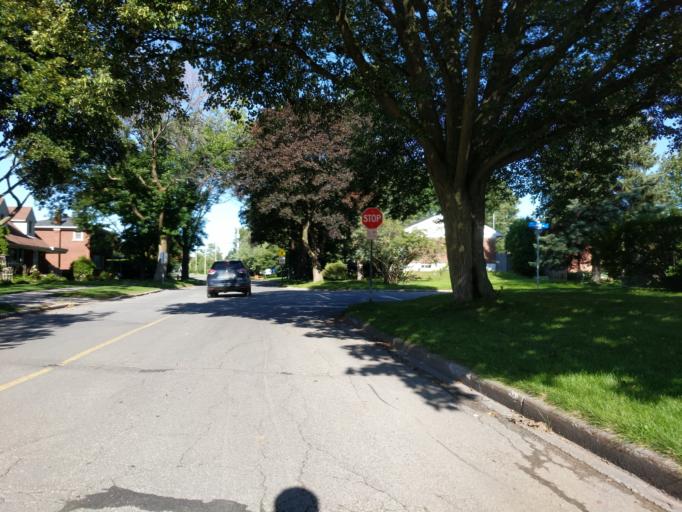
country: CA
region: Ontario
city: Bells Corners
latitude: 45.3616
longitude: -75.7638
